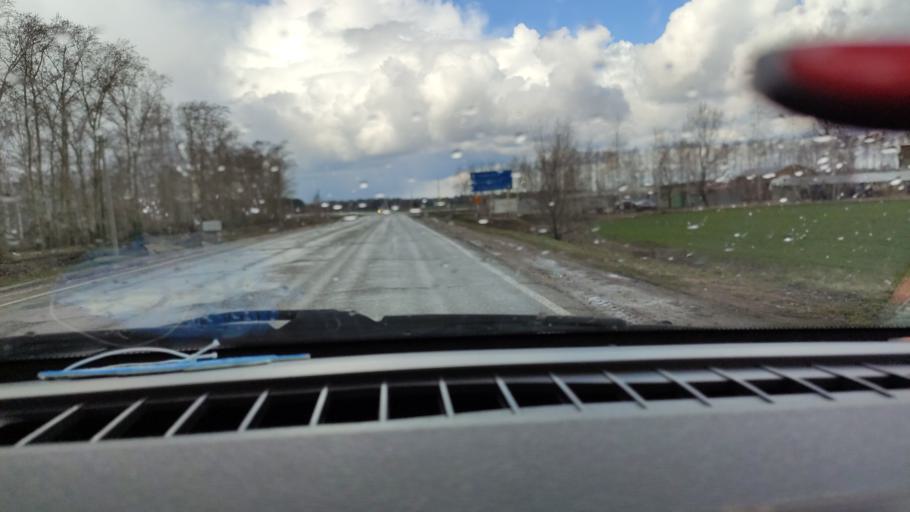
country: RU
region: Samara
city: Povolzhskiy
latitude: 53.8068
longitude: 49.7976
